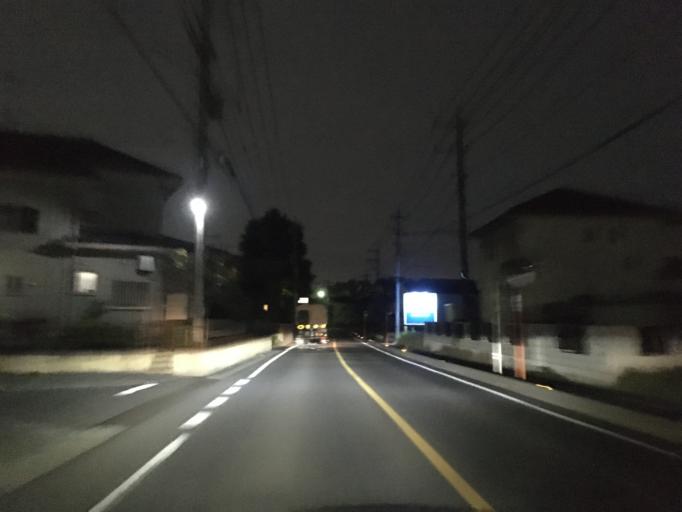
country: JP
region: Saitama
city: Sayama
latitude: 35.8807
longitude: 139.3871
